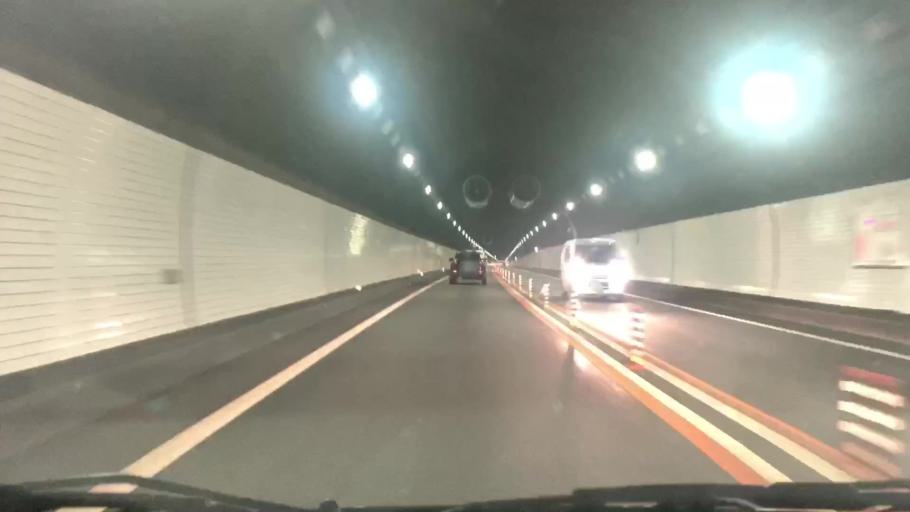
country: JP
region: Nagasaki
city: Nagasaki-shi
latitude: 32.7506
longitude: 129.9266
